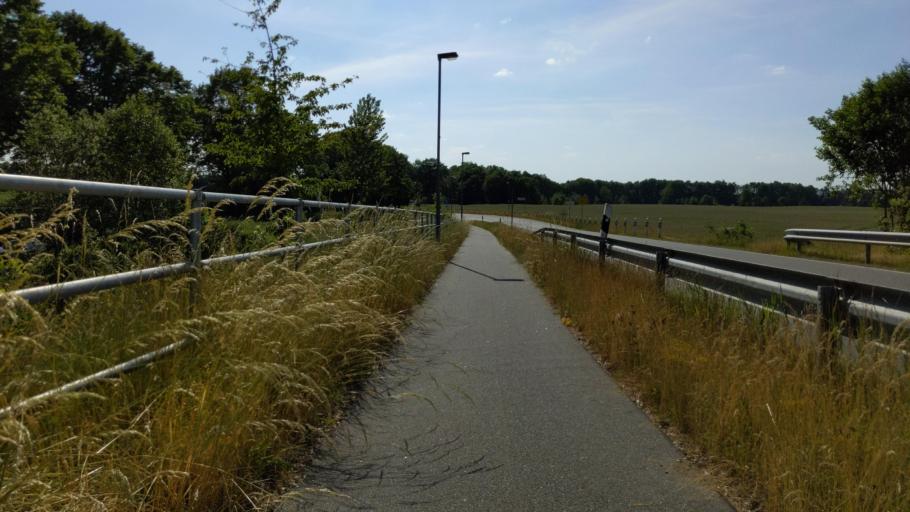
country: DE
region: Schleswig-Holstein
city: Klempau
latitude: 53.8041
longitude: 10.6947
